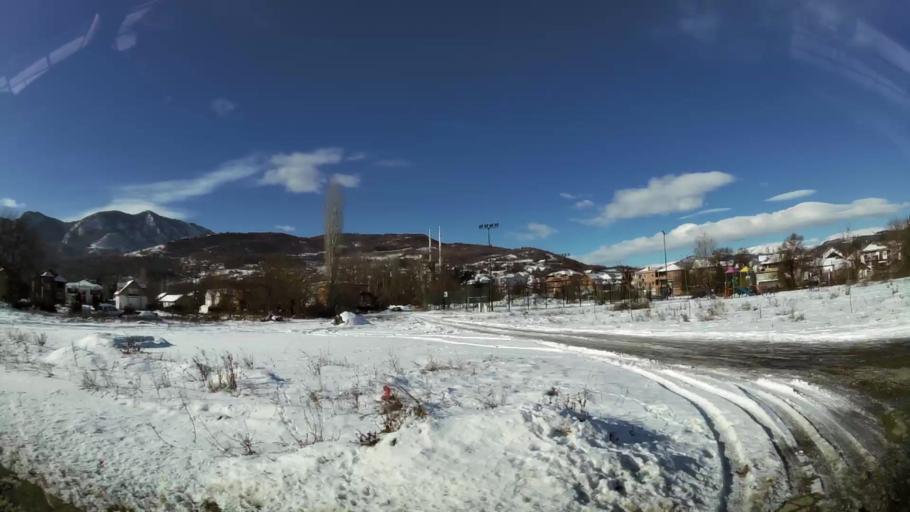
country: MK
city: Ljubin
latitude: 41.9798
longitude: 21.3089
